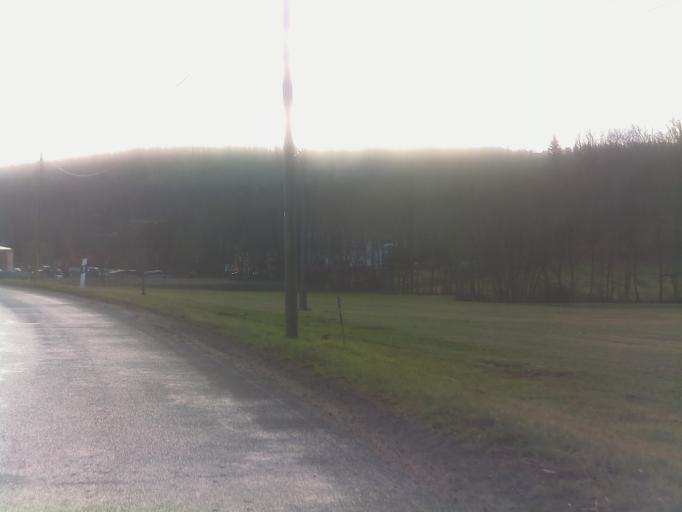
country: DE
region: Thuringia
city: Rottenbach
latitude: 50.6990
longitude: 11.2069
